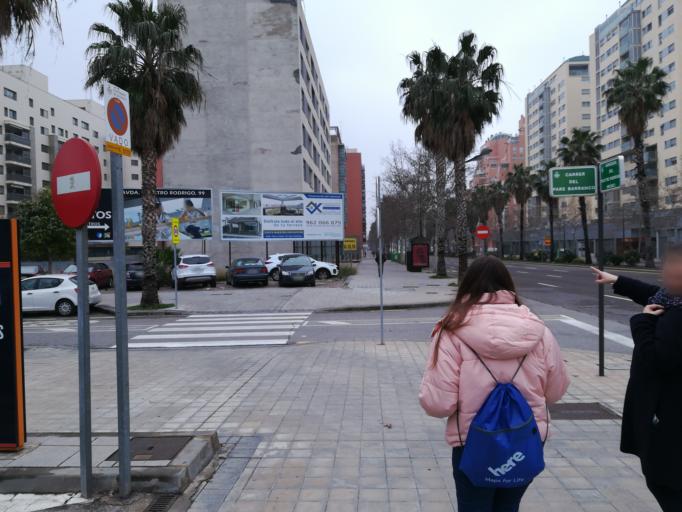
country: ES
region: Valencia
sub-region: Provincia de Valencia
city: Mislata
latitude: 39.4875
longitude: -0.4045
